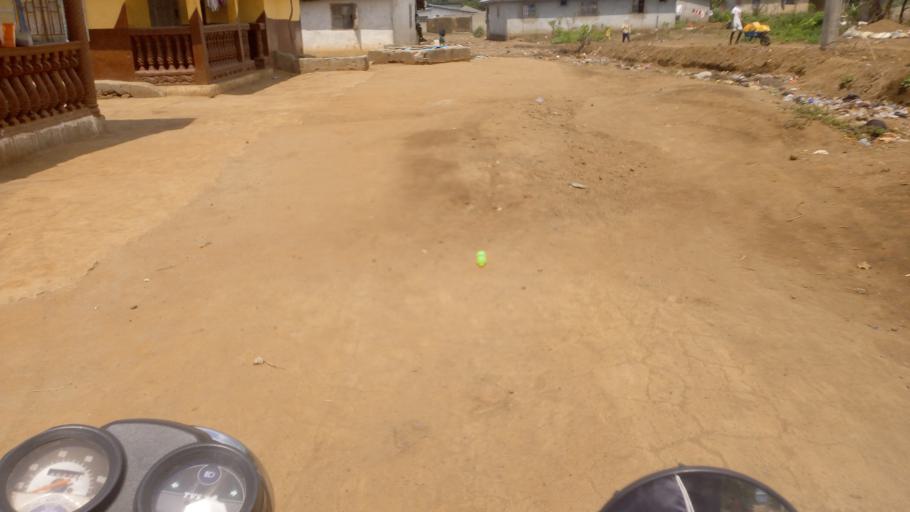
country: SL
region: Western Area
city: Waterloo
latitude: 8.3274
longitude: -13.0775
